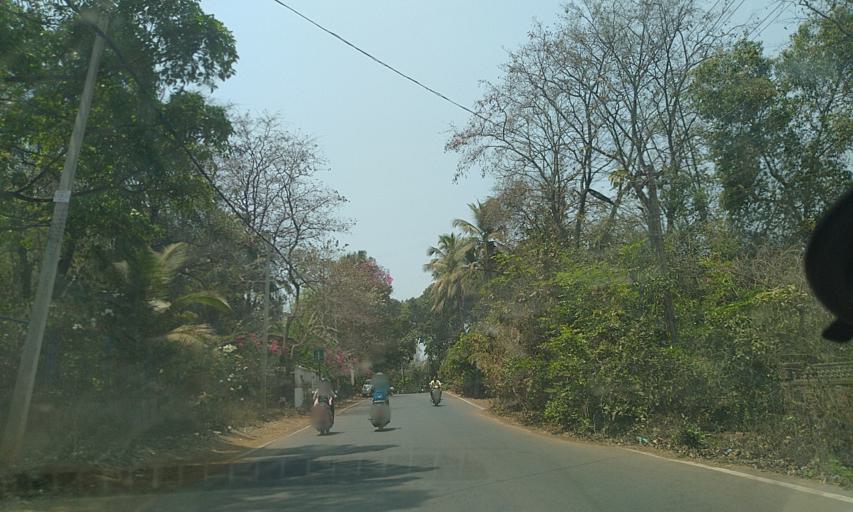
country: IN
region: Goa
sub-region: North Goa
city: Mapuca
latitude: 15.5972
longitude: 73.7889
